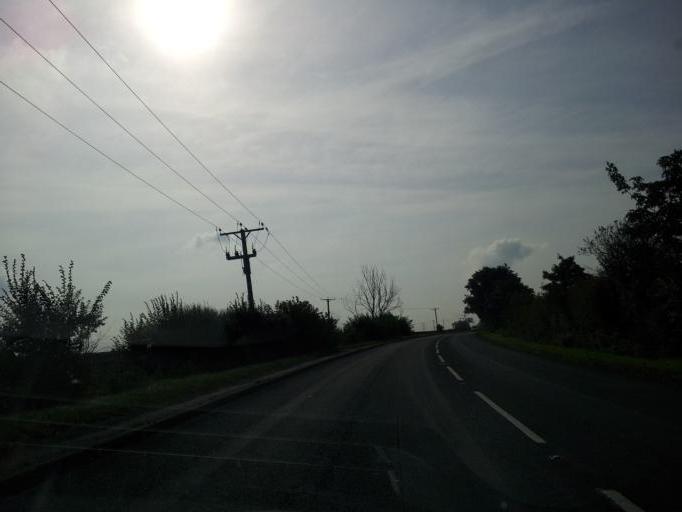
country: GB
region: England
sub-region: Lincolnshire
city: Long Bennington
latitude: 53.0410
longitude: -0.7710
